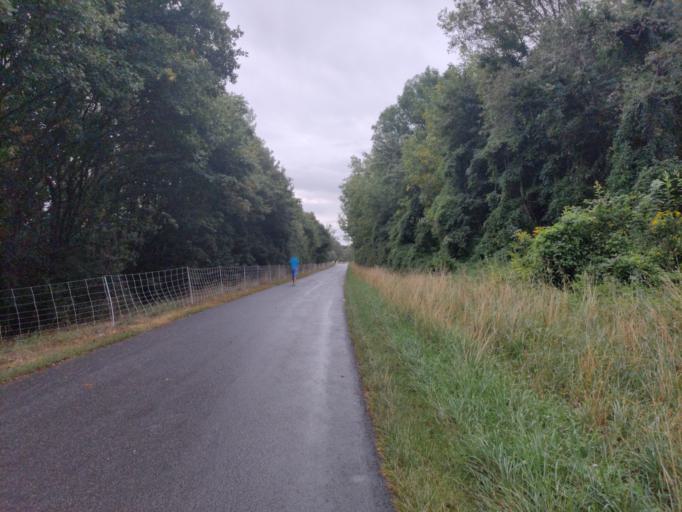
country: AT
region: Lower Austria
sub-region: Politischer Bezirk Korneuburg
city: Langenzersdorf
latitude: 48.2932
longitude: 16.3500
